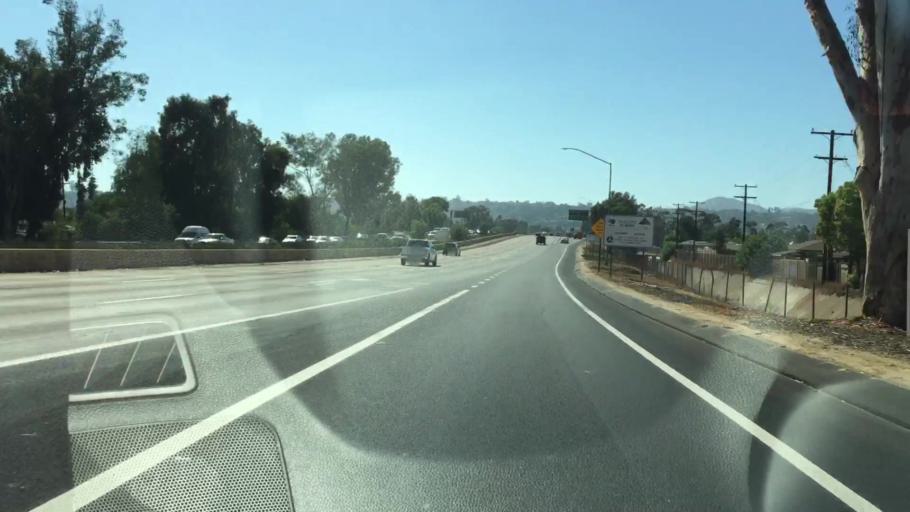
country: US
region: California
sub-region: San Diego County
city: El Cajon
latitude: 32.8032
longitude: -116.9544
